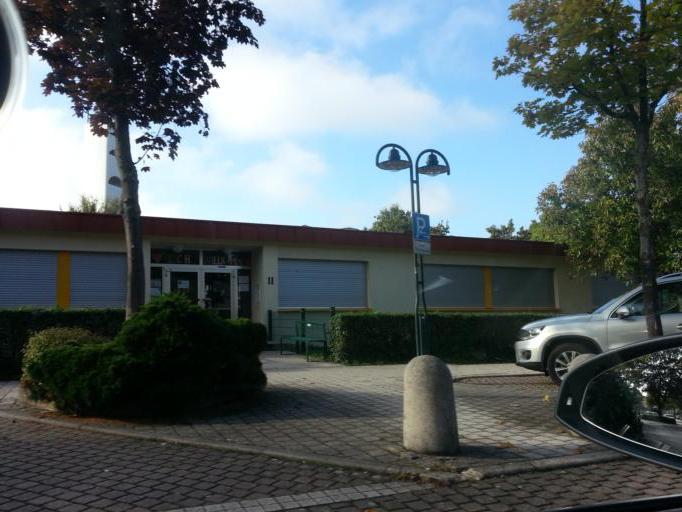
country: DE
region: Baden-Wuerttemberg
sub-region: Karlsruhe Region
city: Sinsheim
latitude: 49.2550
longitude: 8.8756
